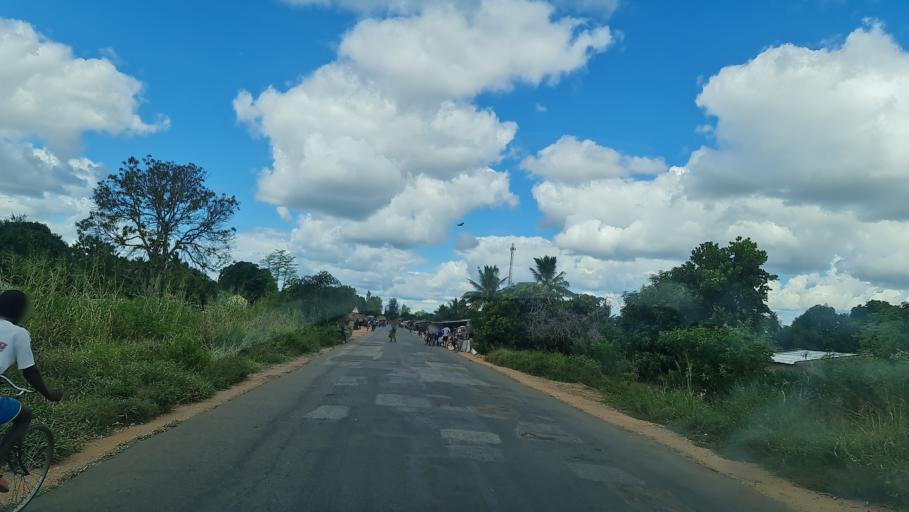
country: MZ
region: Zambezia
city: Quelimane
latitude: -17.5200
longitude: 36.2643
